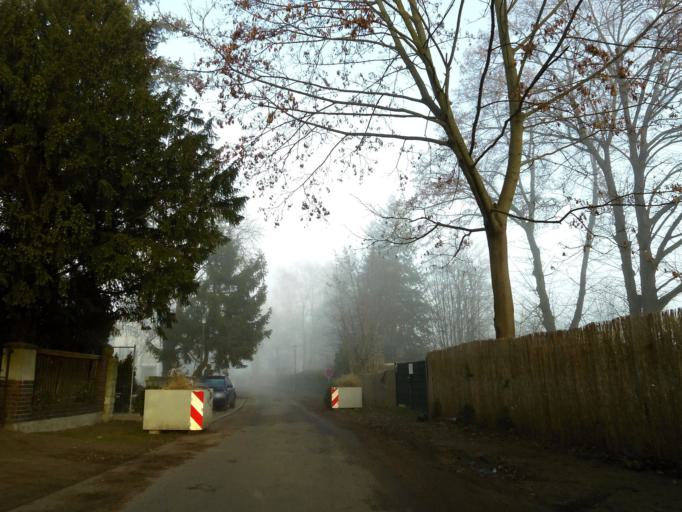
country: DE
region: Brandenburg
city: Werder
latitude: 52.3584
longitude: 12.9879
